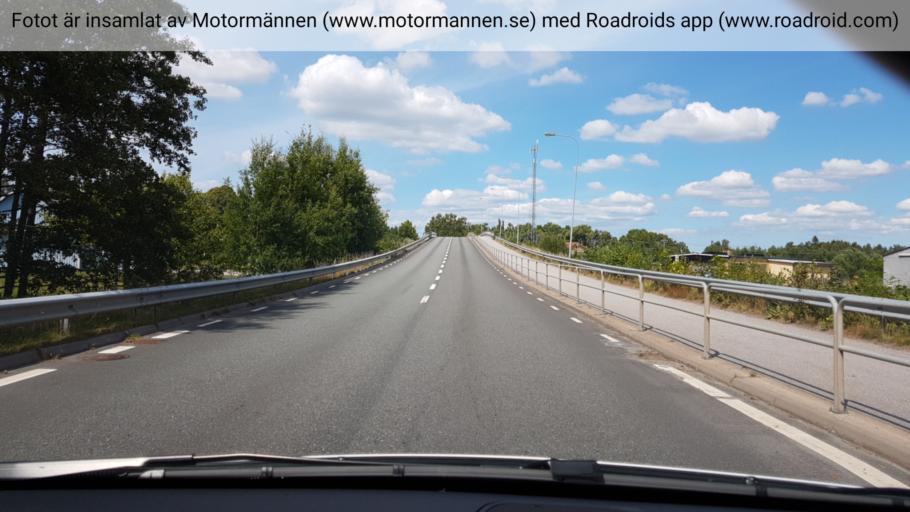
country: SE
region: Vaestra Goetaland
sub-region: Toreboda Kommun
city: Toereboda
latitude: 58.6054
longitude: 14.0410
